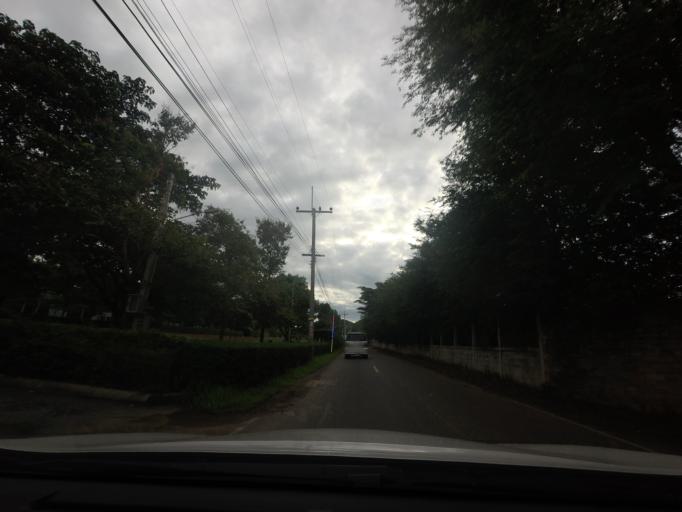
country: TH
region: Nakhon Ratchasima
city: Pak Chong
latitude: 14.6055
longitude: 101.4321
